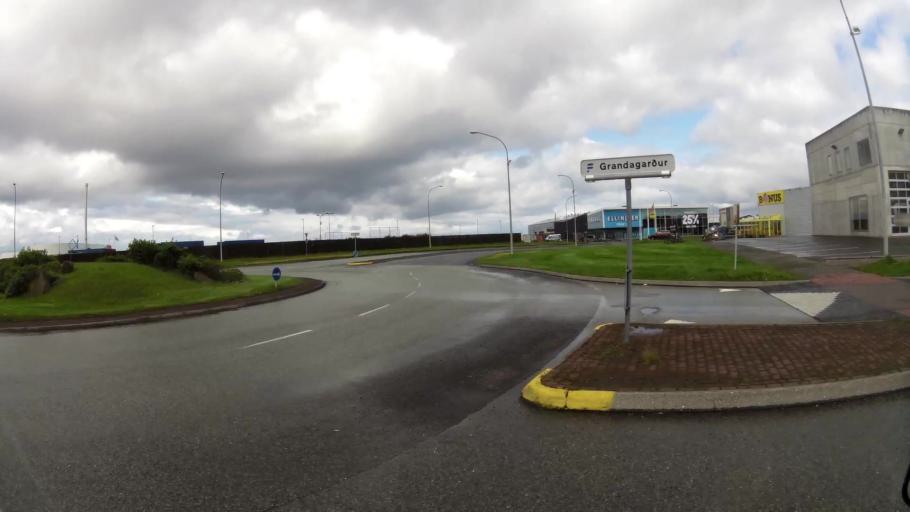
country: IS
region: Capital Region
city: Seltjarnarnes
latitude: 64.1528
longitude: -21.9522
